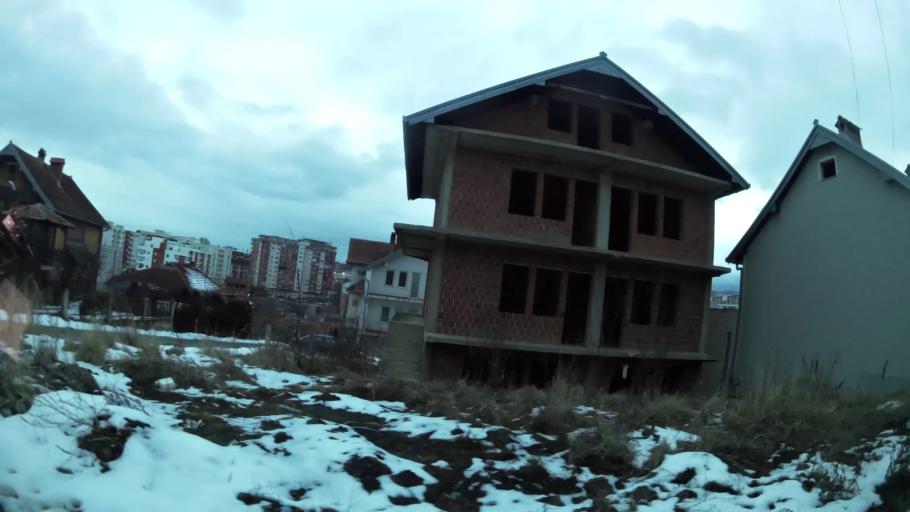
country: XK
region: Pristina
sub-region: Komuna e Prishtines
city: Pristina
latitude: 42.6406
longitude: 21.1682
